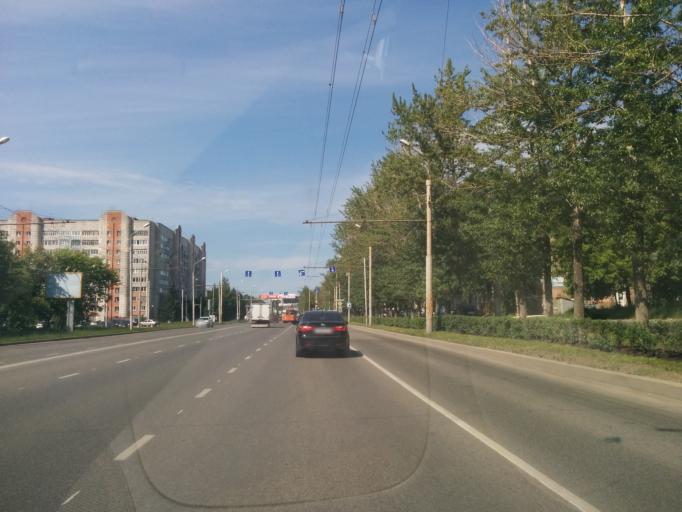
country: RU
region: Perm
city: Perm
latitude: 57.9963
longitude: 56.2877
